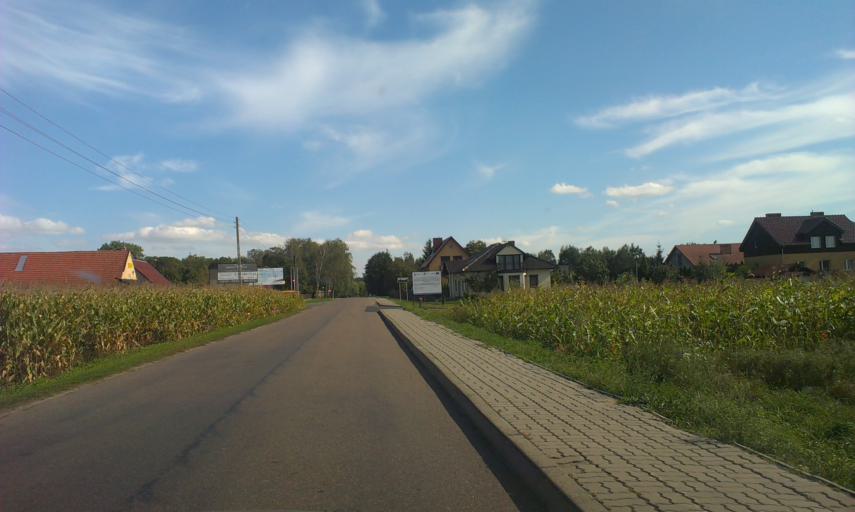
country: PL
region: Greater Poland Voivodeship
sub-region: Powiat pilski
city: Lobzenica
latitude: 53.2697
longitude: 17.2496
